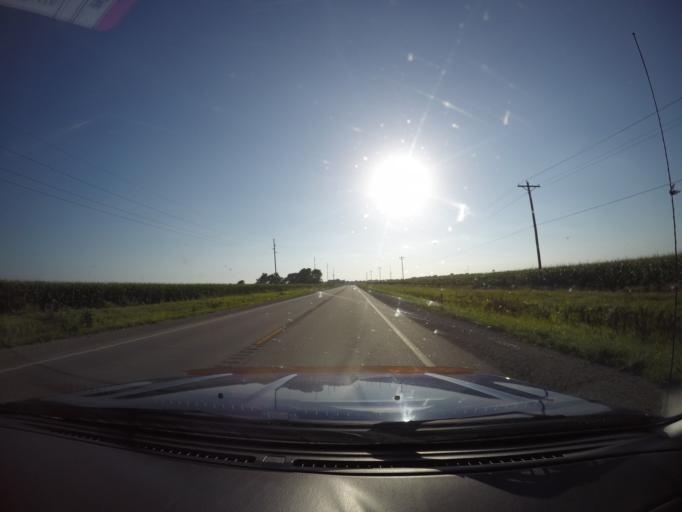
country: US
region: Kansas
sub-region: Shawnee County
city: Silver Lake
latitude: 39.0941
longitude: -95.8317
